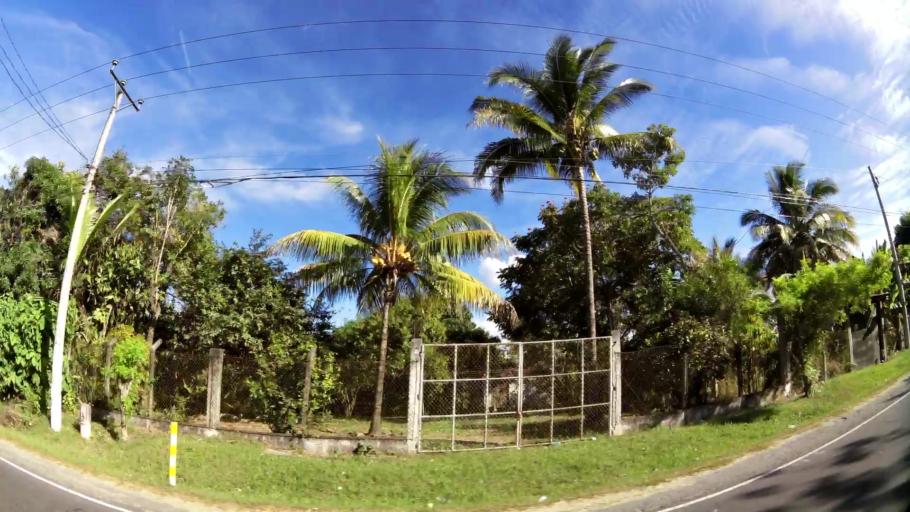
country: SV
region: Cuscatlan
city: Tecoluca
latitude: 13.7880
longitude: -89.0458
